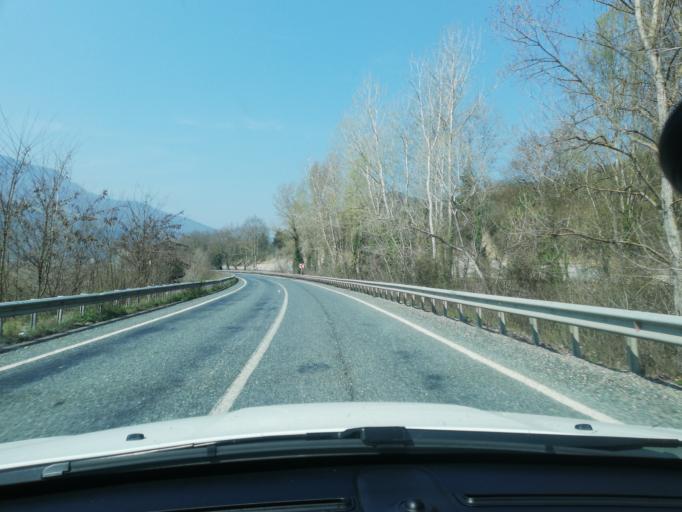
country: TR
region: Karabuk
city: Yenice
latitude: 41.2178
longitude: 32.2911
